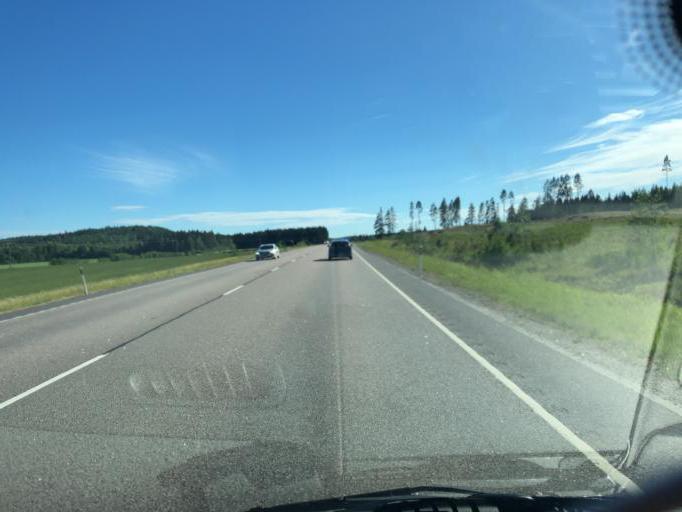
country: FI
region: Kymenlaakso
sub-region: Kouvola
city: Elimaeki
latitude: 60.7847
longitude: 26.4945
